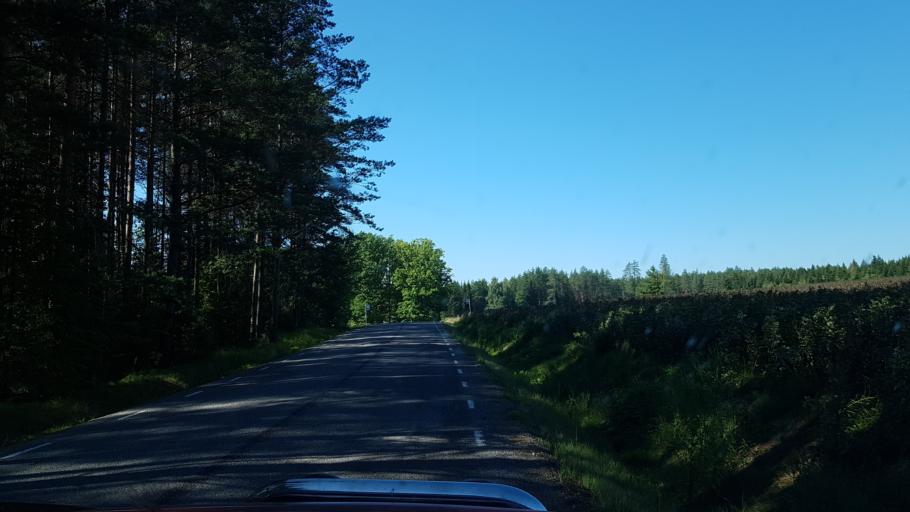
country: EE
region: Polvamaa
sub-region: Polva linn
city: Polva
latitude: 58.2110
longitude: 27.1473
